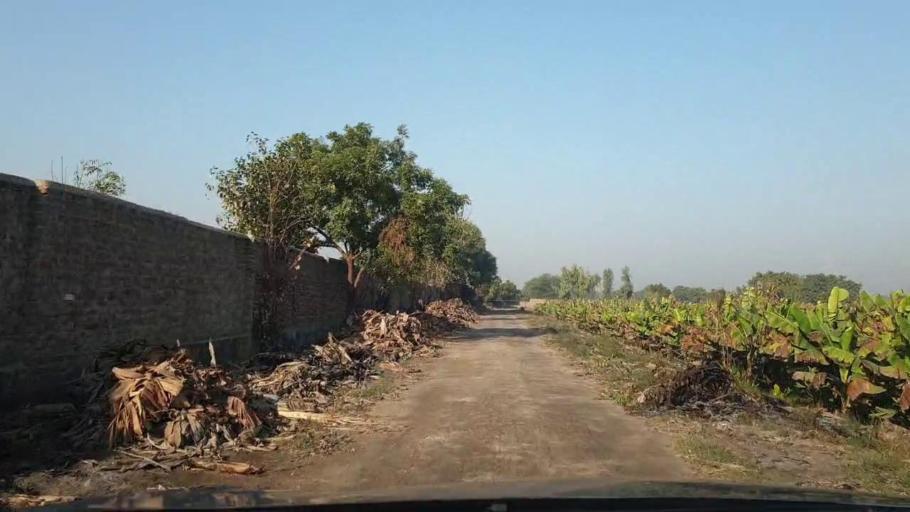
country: PK
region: Sindh
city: Tando Allahyar
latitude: 25.4916
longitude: 68.7125
